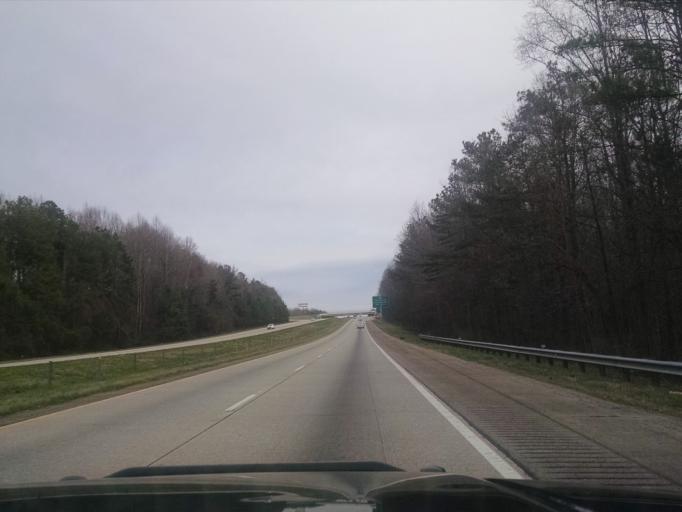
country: US
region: Georgia
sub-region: Gwinnett County
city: Buford
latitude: 34.1345
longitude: -83.9559
